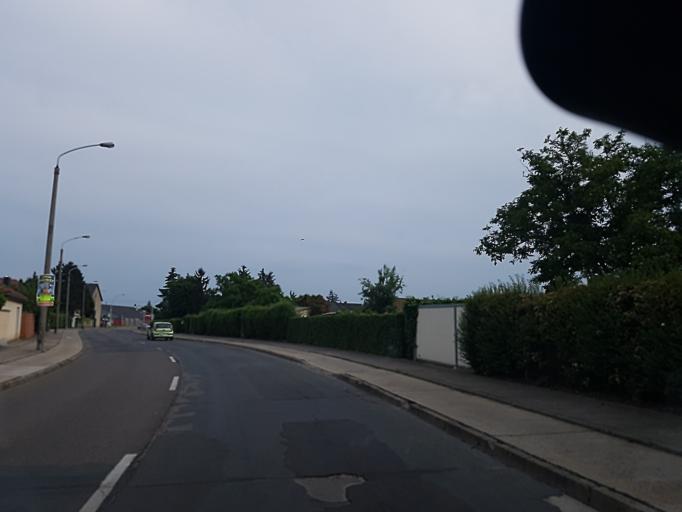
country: DE
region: Saxony-Anhalt
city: Wittenburg
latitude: 51.8771
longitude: 12.6670
